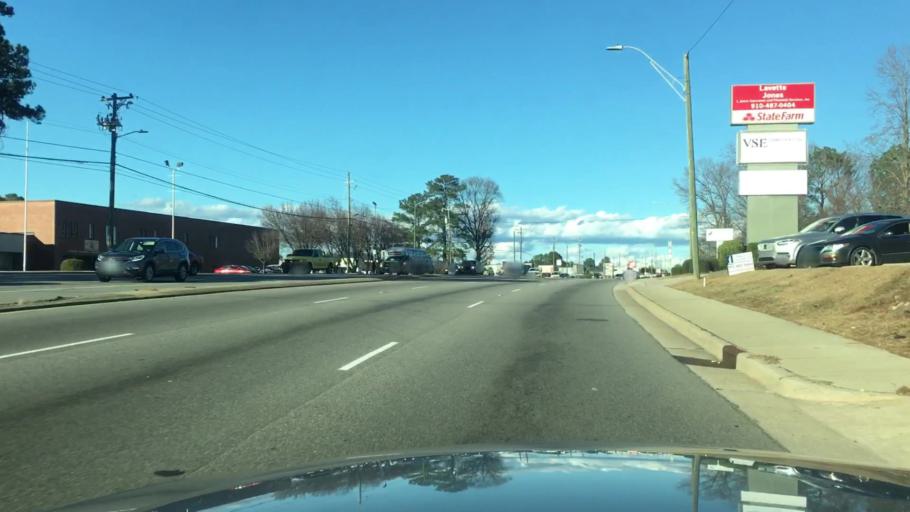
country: US
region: North Carolina
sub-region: Cumberland County
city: Hope Mills
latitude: 35.0476
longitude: -78.9757
